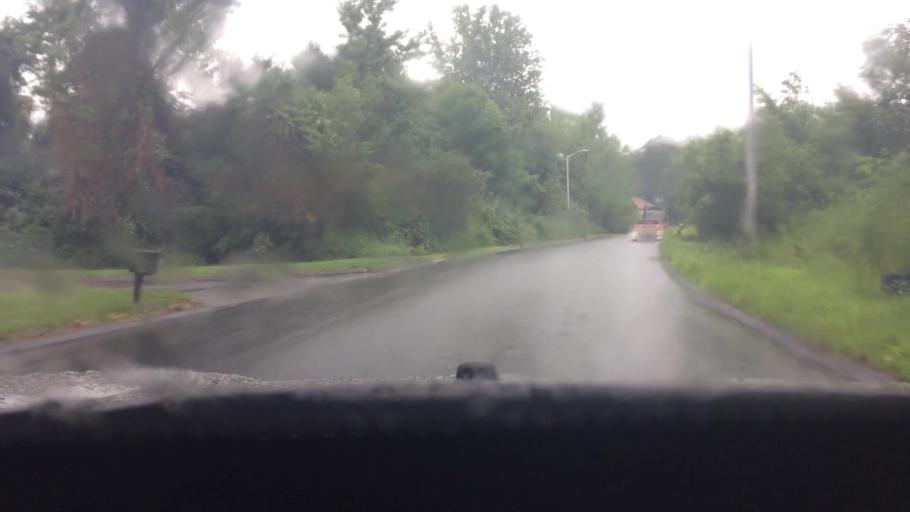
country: US
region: Connecticut
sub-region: Hartford County
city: Tariffville
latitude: 41.8590
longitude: -72.7367
